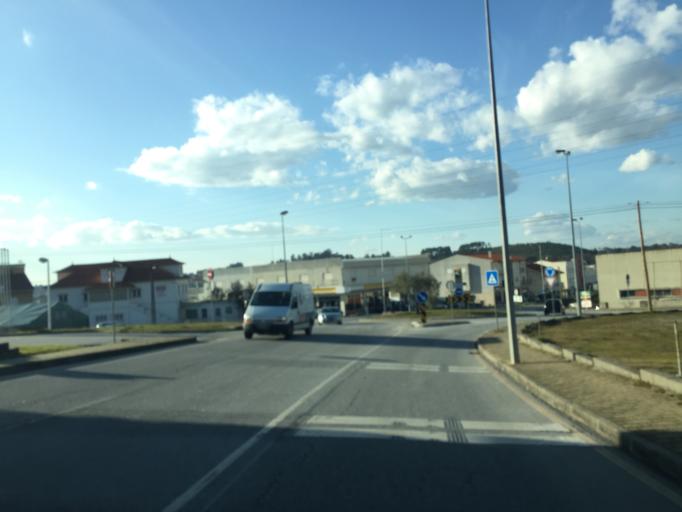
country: PT
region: Guarda
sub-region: Seia
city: Seia
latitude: 40.4210
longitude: -7.7123
